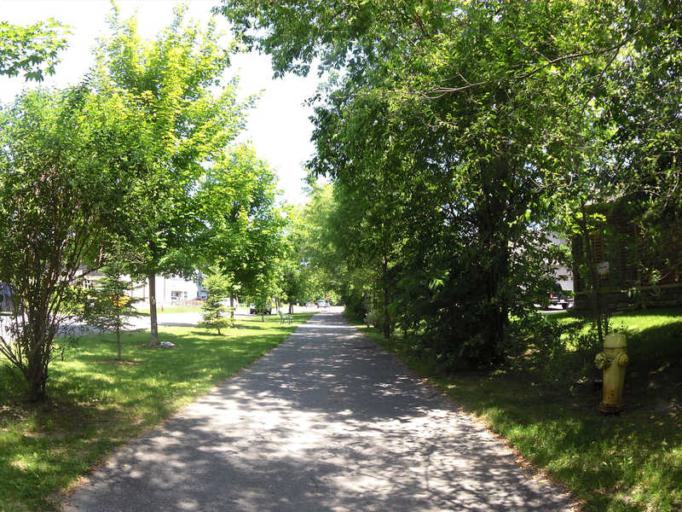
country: CA
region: Ontario
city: Peterborough
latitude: 44.4235
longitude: -78.2693
